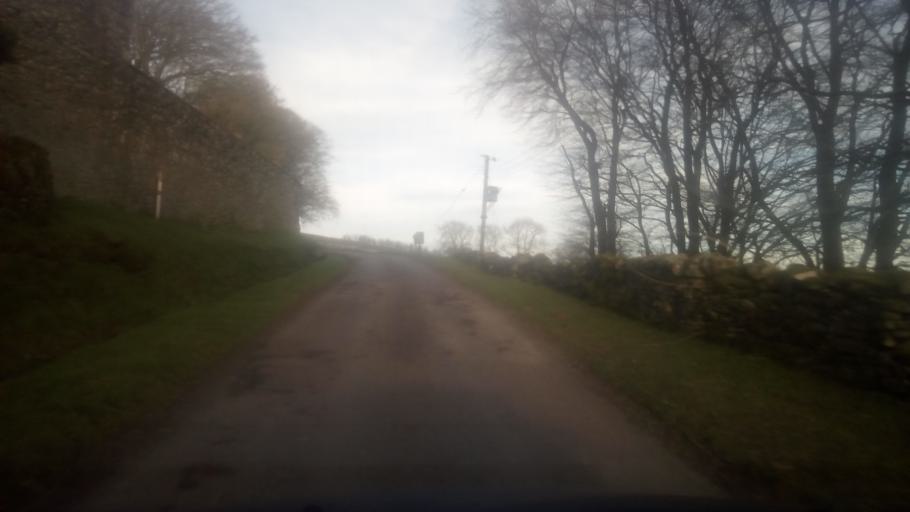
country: GB
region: Scotland
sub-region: The Scottish Borders
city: Jedburgh
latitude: 55.3897
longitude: -2.5810
